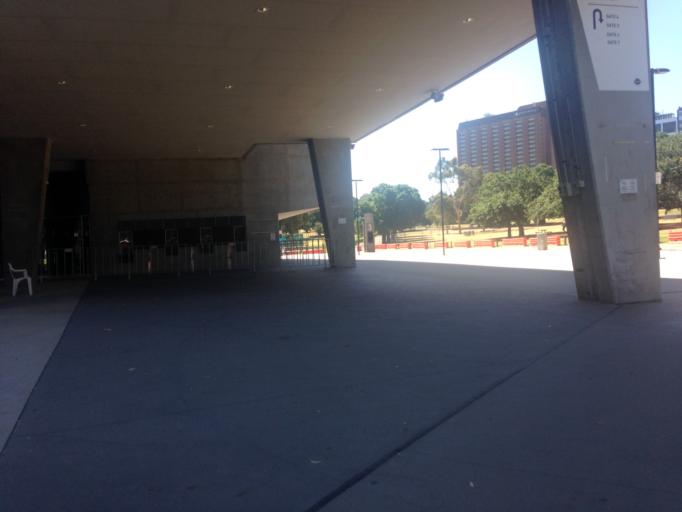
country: AU
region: Victoria
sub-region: Melbourne
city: East Melbourne
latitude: -37.8193
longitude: 144.9849
